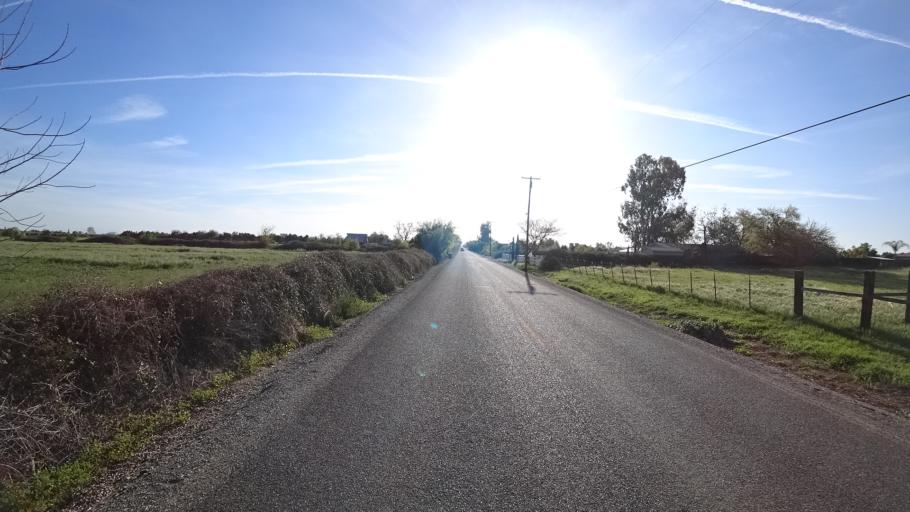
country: US
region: California
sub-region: Glenn County
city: Orland
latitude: 39.7260
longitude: -122.2245
